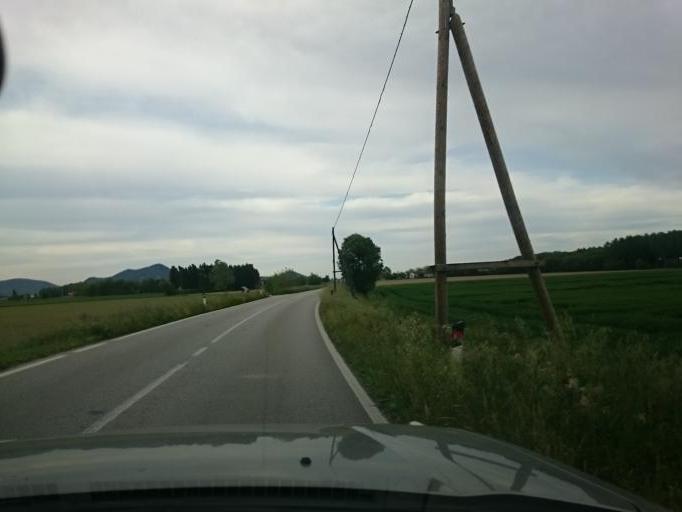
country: IT
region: Veneto
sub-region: Provincia di Padova
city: Sant'Elena
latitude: 45.1983
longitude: 11.7172
